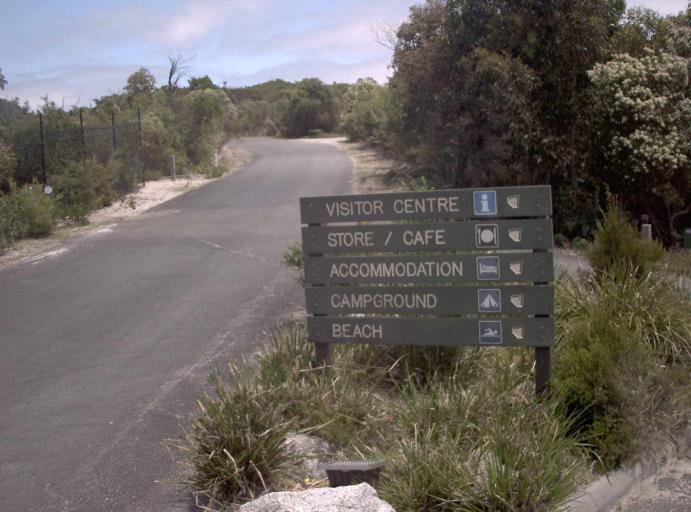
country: AU
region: Victoria
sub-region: Latrobe
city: Morwell
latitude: -39.0308
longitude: 146.3257
